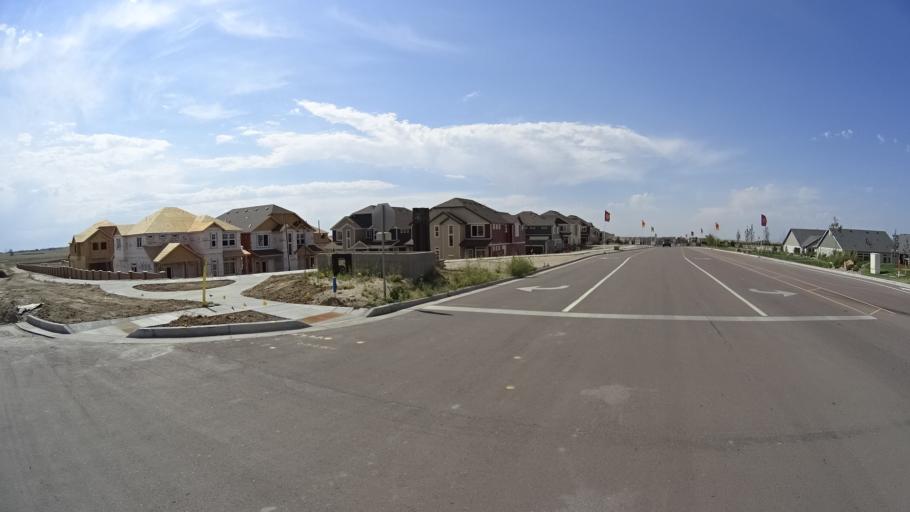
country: US
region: Colorado
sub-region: El Paso County
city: Cimarron Hills
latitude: 38.9263
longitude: -104.6566
